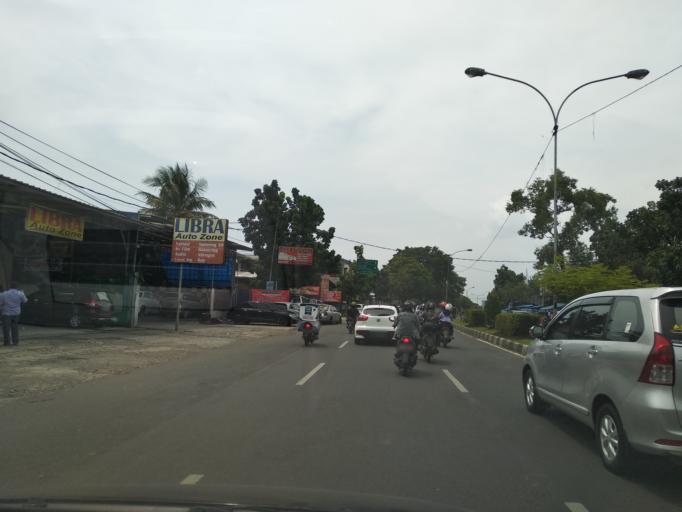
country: ID
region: West Java
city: Bandung
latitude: -6.9372
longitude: 107.6009
